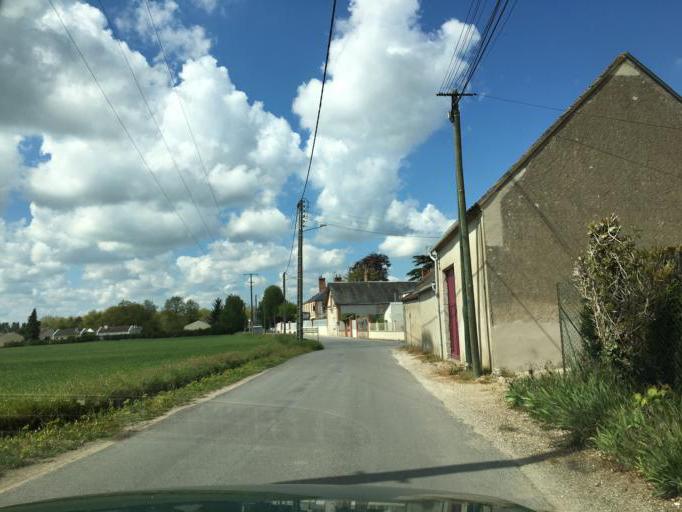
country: FR
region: Centre
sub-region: Departement du Loiret
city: Clery-Saint-Andre
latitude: 47.8194
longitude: 1.7613
